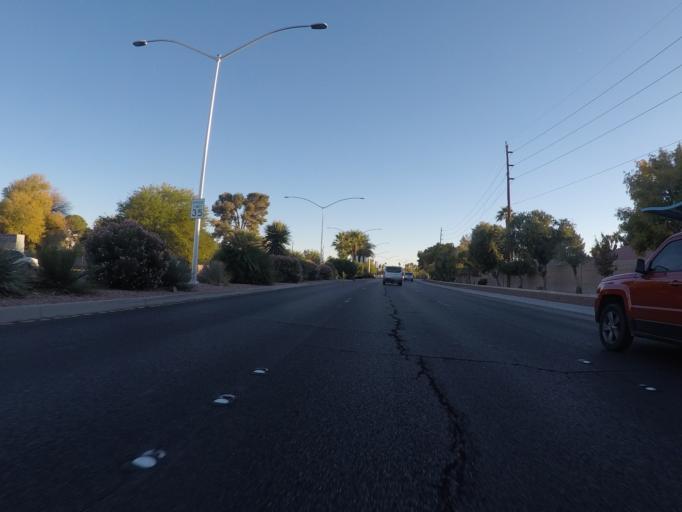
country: US
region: Nevada
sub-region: Clark County
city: Las Vegas
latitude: 36.1731
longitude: -115.1732
